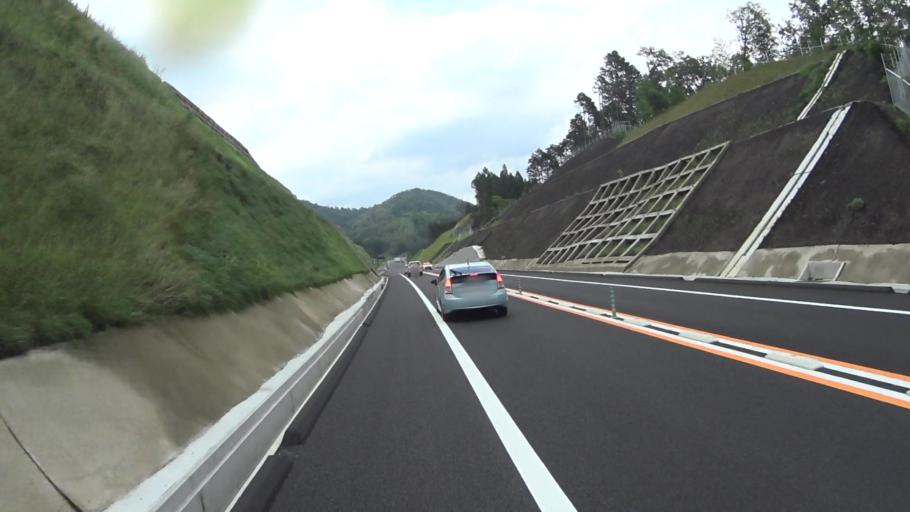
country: JP
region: Kyoto
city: Ayabe
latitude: 35.1998
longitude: 135.3548
